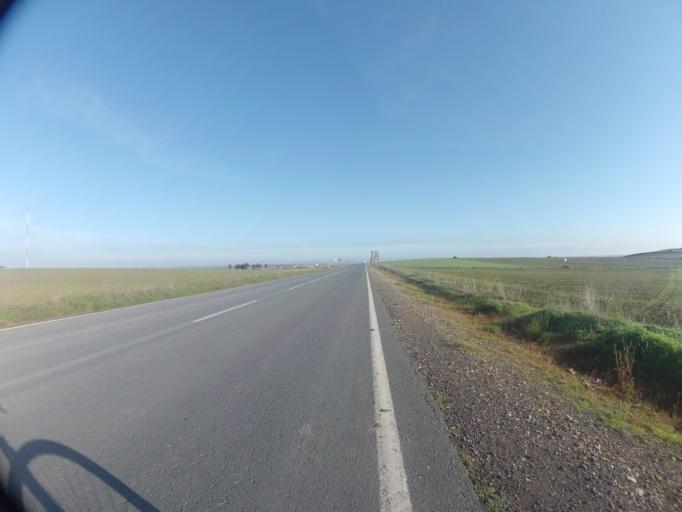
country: ES
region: Andalusia
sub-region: Provincia de Huelva
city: Huelva
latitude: 37.3027
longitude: -6.9248
